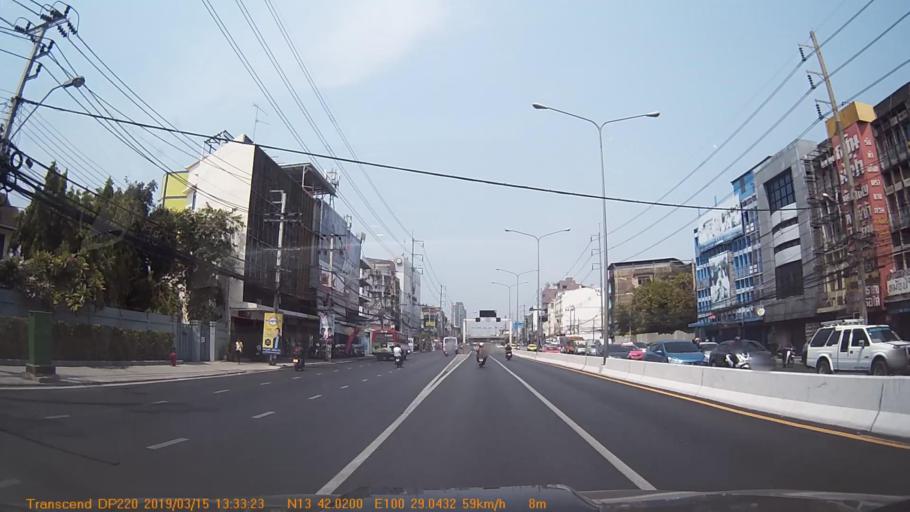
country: TH
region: Bangkok
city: Bang Kho Laem
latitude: 13.7006
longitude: 100.4841
